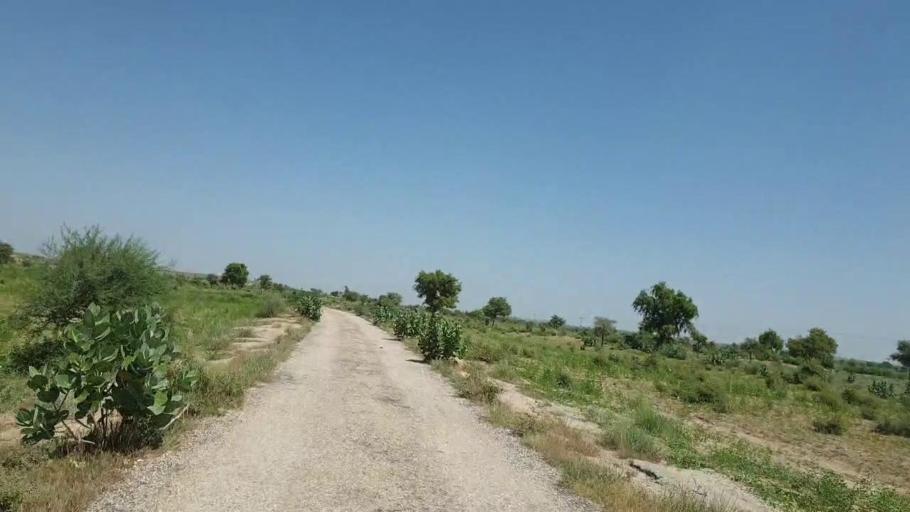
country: PK
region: Sindh
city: Islamkot
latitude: 25.1408
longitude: 70.3965
